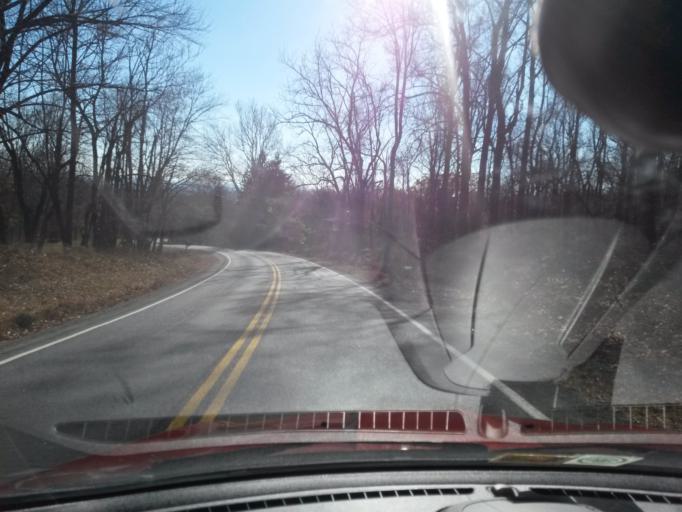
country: US
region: Virginia
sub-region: City of Bedford
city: Bedford
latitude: 37.4308
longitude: -79.5753
